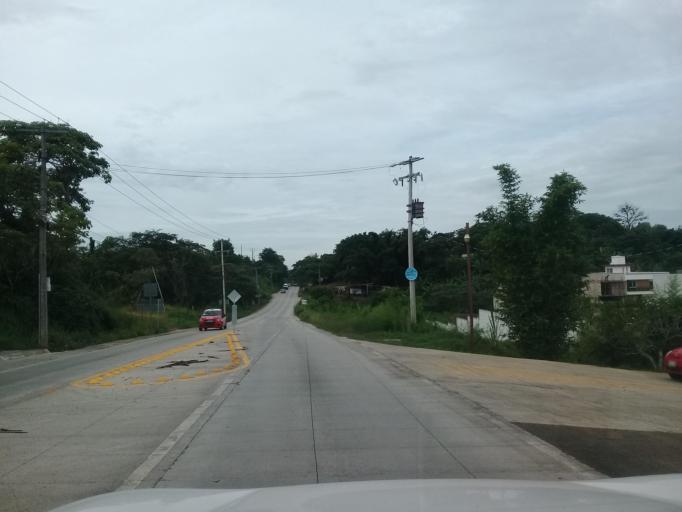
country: MX
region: Veracruz
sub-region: Emiliano Zapata
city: Jacarandas
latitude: 19.4852
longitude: -96.8577
